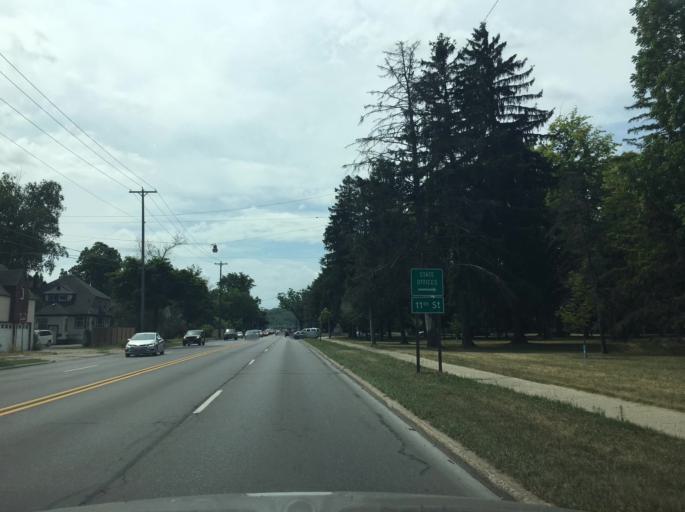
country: US
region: Michigan
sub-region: Grand Traverse County
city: Traverse City
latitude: 44.7568
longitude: -85.6349
